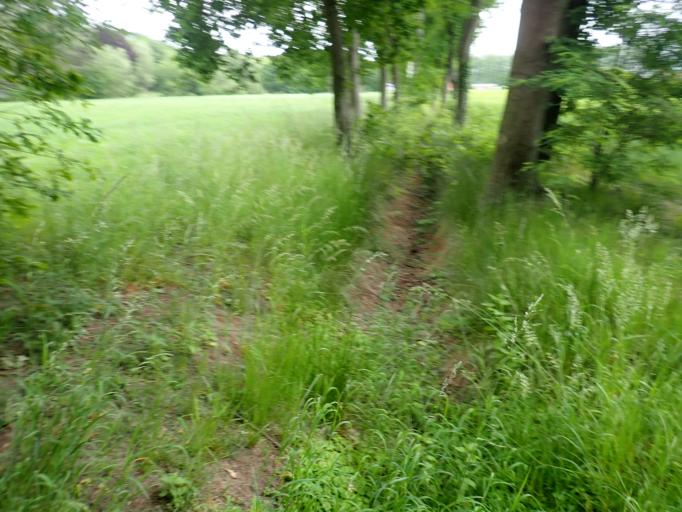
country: BE
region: Flanders
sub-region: Provincie Vlaams-Brabant
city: Haacht
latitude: 50.9793
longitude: 4.6441
